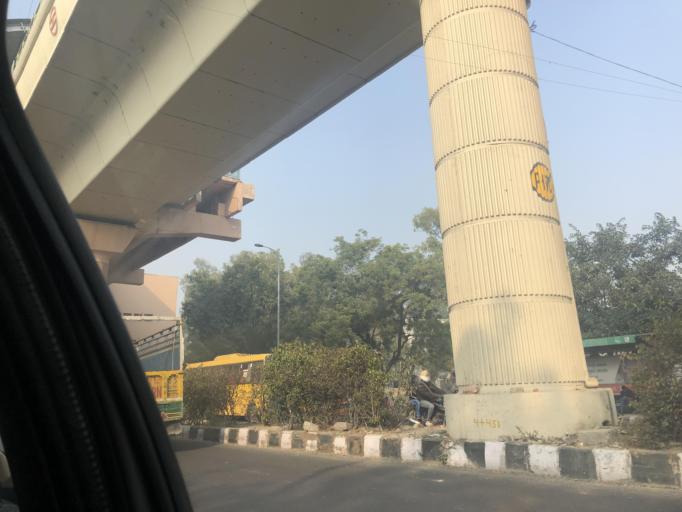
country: IN
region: NCT
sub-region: North West Delhi
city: Pitampura
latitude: 28.6761
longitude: 77.1208
